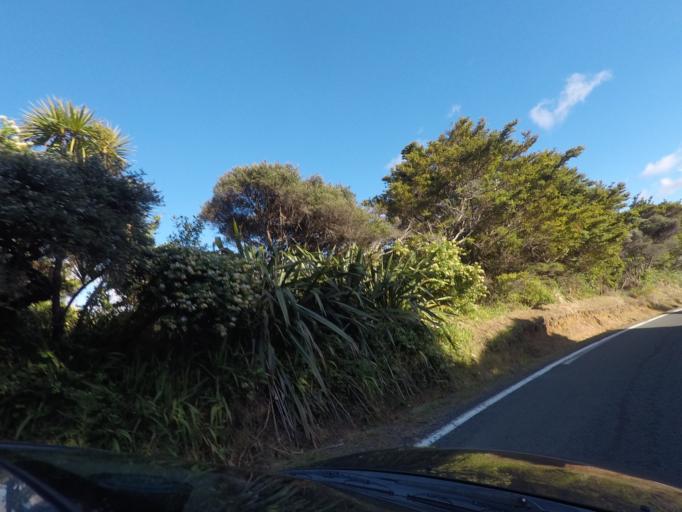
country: NZ
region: Auckland
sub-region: Auckland
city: Titirangi
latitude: -37.0073
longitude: 174.6012
